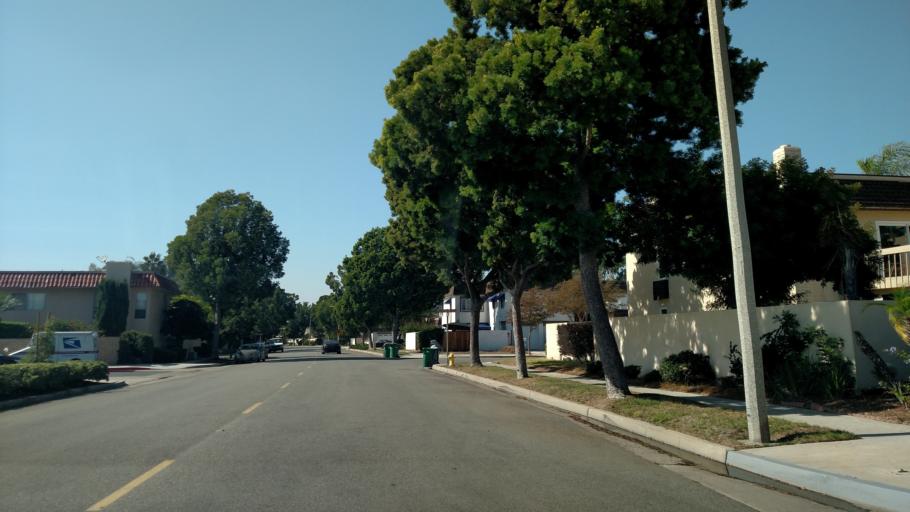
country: US
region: California
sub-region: Orange County
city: Irvine
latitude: 33.6667
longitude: -117.8199
